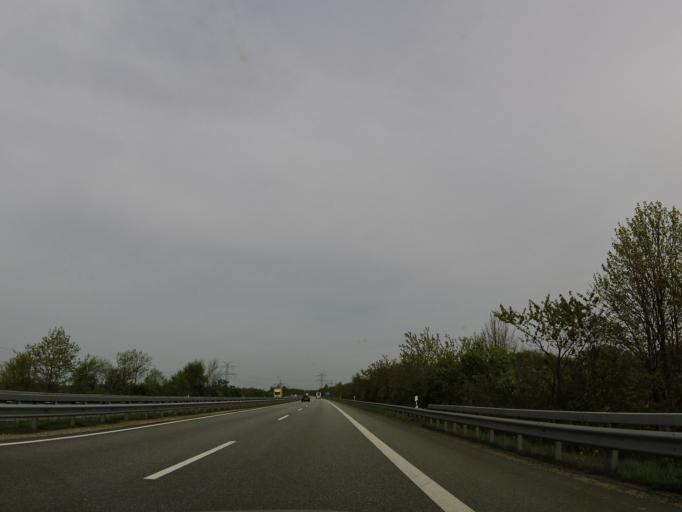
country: DE
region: Schleswig-Holstein
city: Kaaks
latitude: 53.9937
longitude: 9.4876
